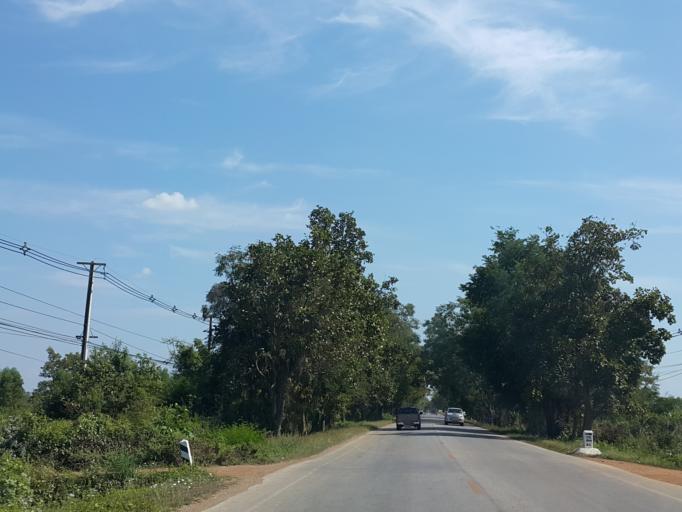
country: TH
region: Sukhothai
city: Sawankhalok
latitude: 17.3089
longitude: 99.7561
